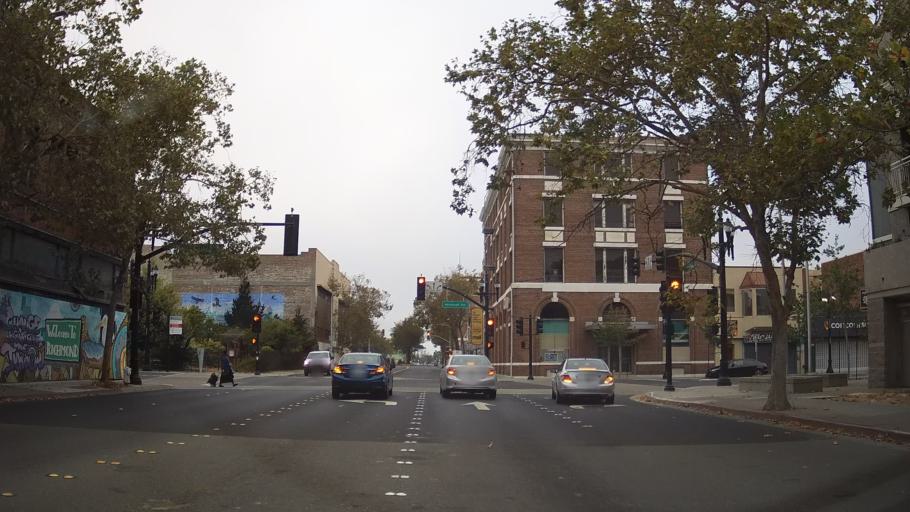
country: US
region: California
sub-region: Contra Costa County
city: Richmond
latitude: 37.9353
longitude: -122.3599
